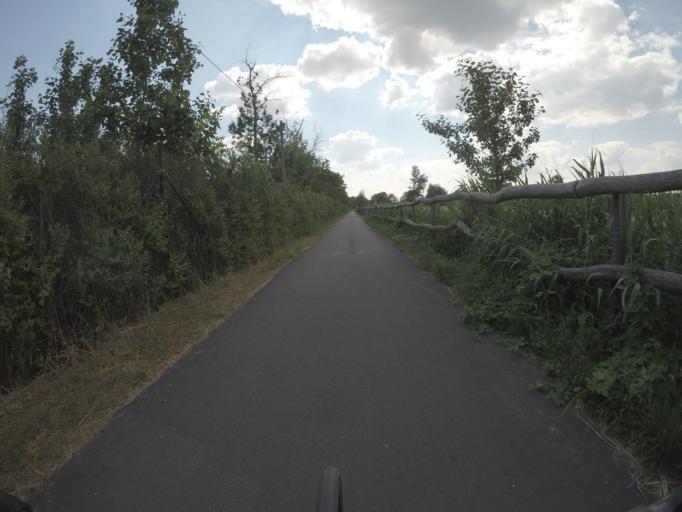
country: DE
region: Brandenburg
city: Roskow
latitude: 52.4553
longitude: 12.7795
